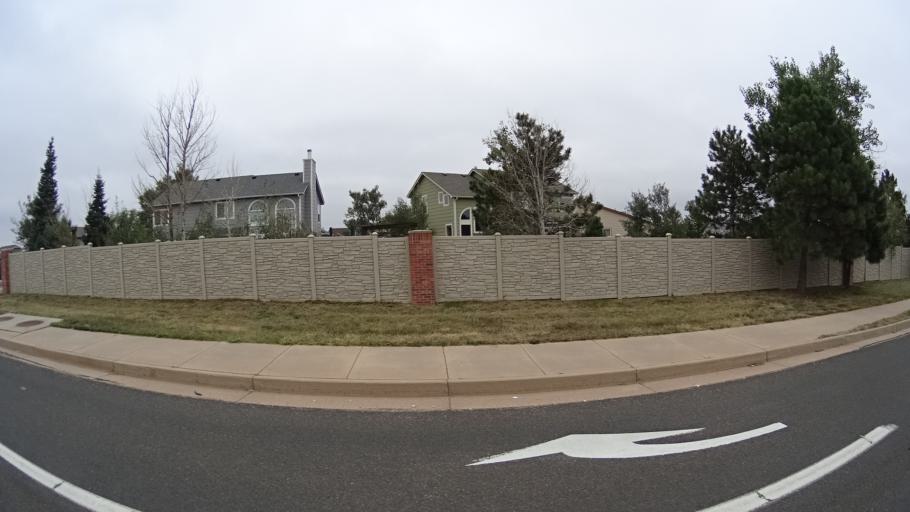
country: US
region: Colorado
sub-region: El Paso County
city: Cimarron Hills
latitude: 38.8931
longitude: -104.7020
